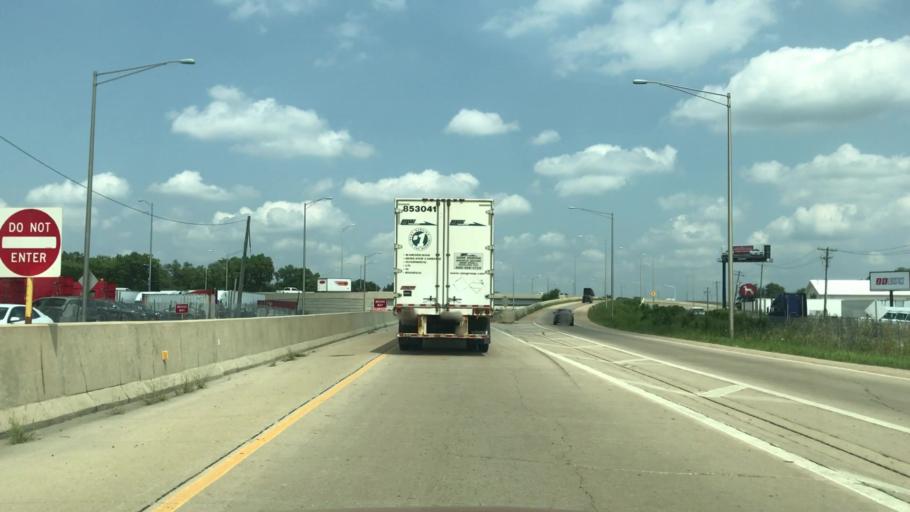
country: US
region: Illinois
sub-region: Will County
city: Bolingbrook
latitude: 41.6972
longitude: -88.0418
